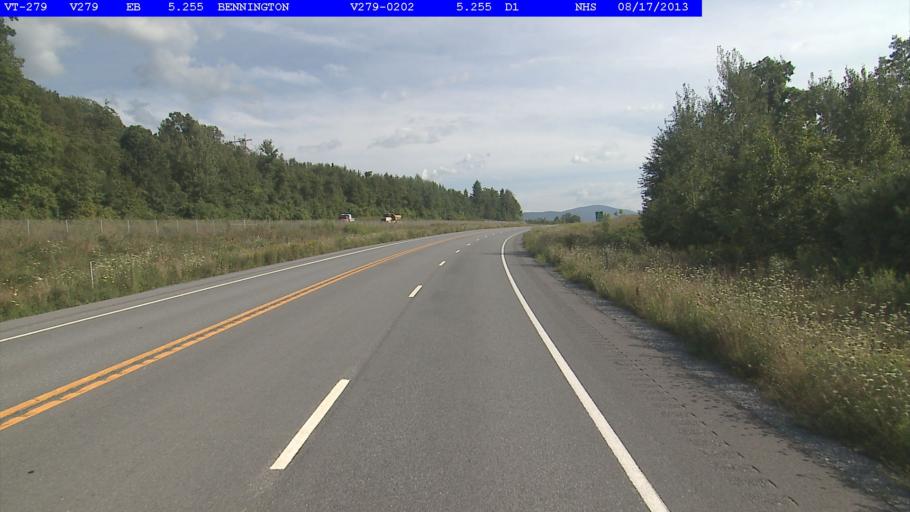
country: US
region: Vermont
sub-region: Bennington County
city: Bennington
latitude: 42.8980
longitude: -73.1771
